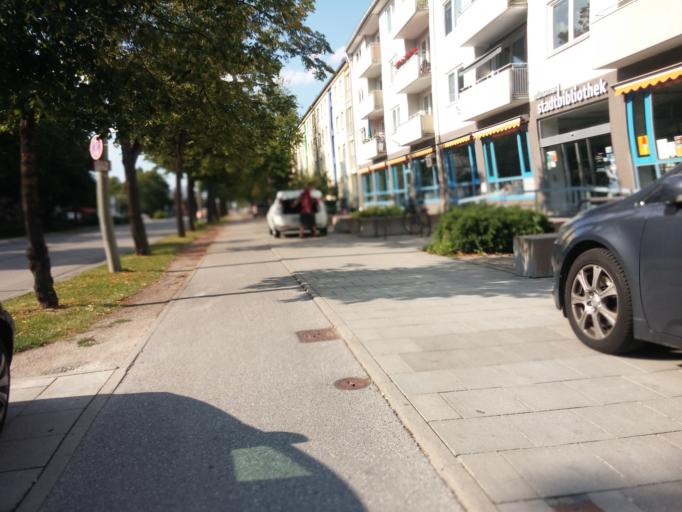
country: DE
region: Bavaria
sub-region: Upper Bavaria
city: Munich
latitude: 48.1827
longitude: 11.5669
